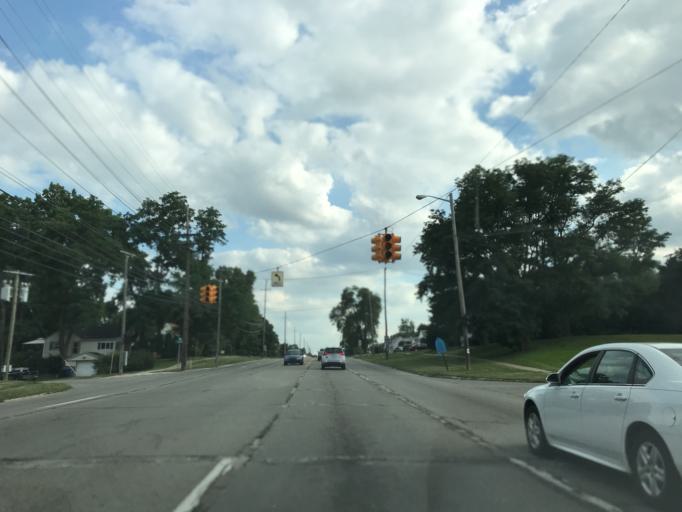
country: US
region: Michigan
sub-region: Wayne County
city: Redford
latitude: 42.4070
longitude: -83.2963
